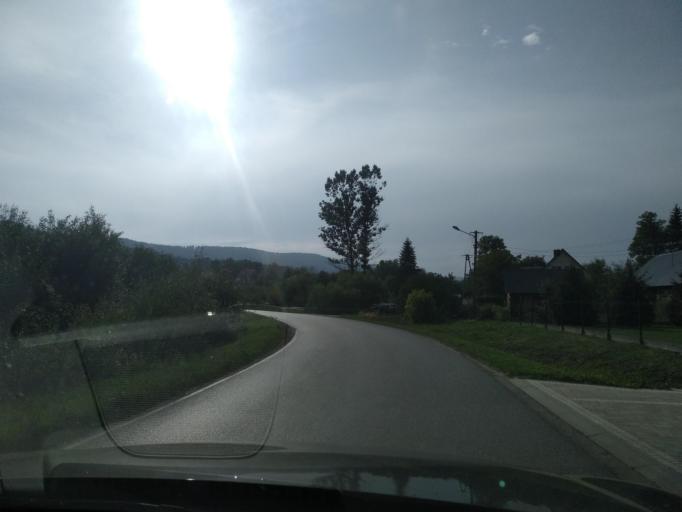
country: PL
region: Subcarpathian Voivodeship
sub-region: Powiat sanocki
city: Tyrawa Woloska
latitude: 49.5390
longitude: 22.4165
